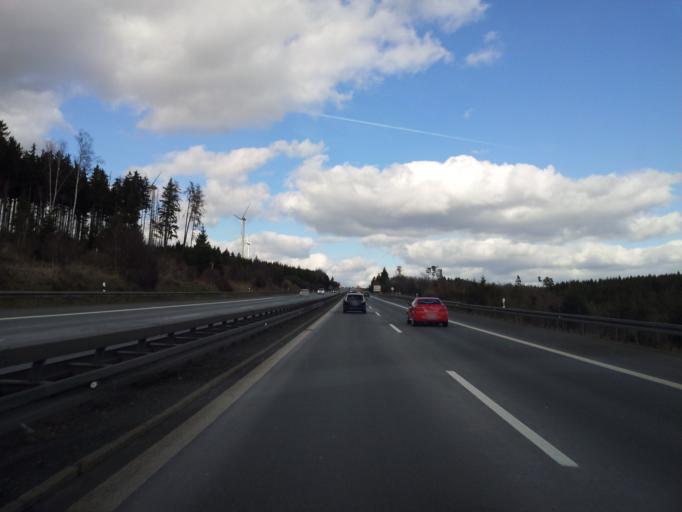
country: DE
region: Bavaria
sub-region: Upper Franconia
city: Topen
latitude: 50.3568
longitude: 11.8705
